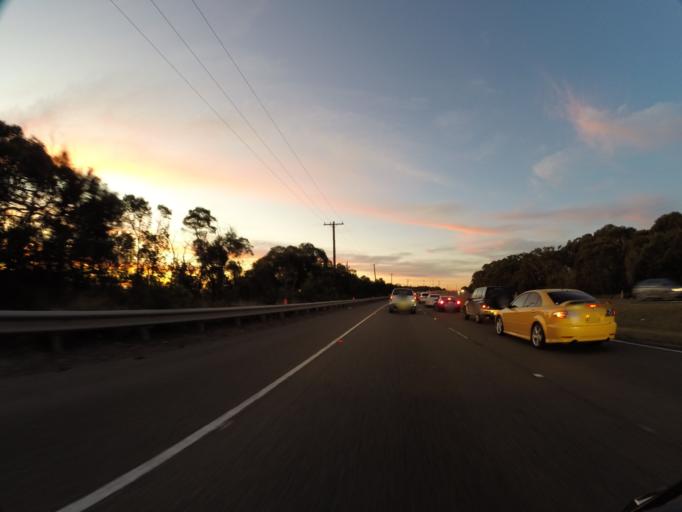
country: AU
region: New South Wales
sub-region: Sutherland Shire
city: Heathcote
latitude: -34.1157
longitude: 150.9916
